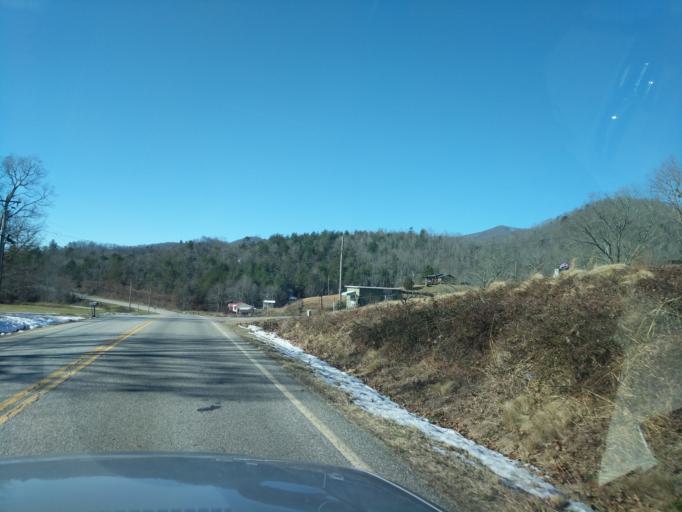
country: US
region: Georgia
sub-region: Towns County
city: Hiawassee
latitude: 34.9303
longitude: -83.6507
